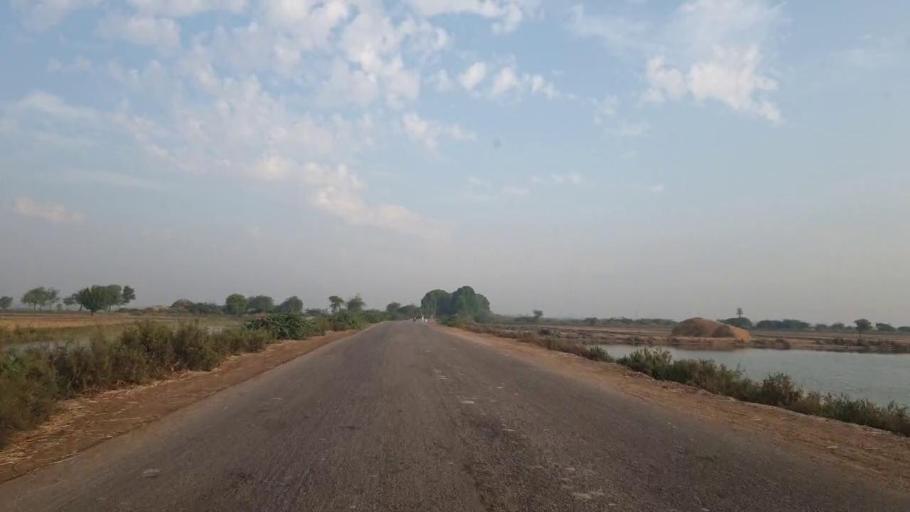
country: PK
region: Sindh
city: Tando Bago
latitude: 24.7245
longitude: 68.9425
